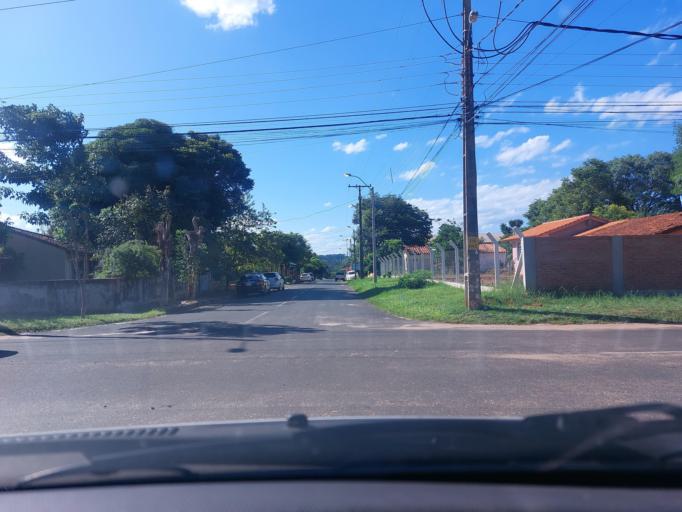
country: PY
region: San Pedro
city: Guayaybi
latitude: -24.6611
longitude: -56.4440
